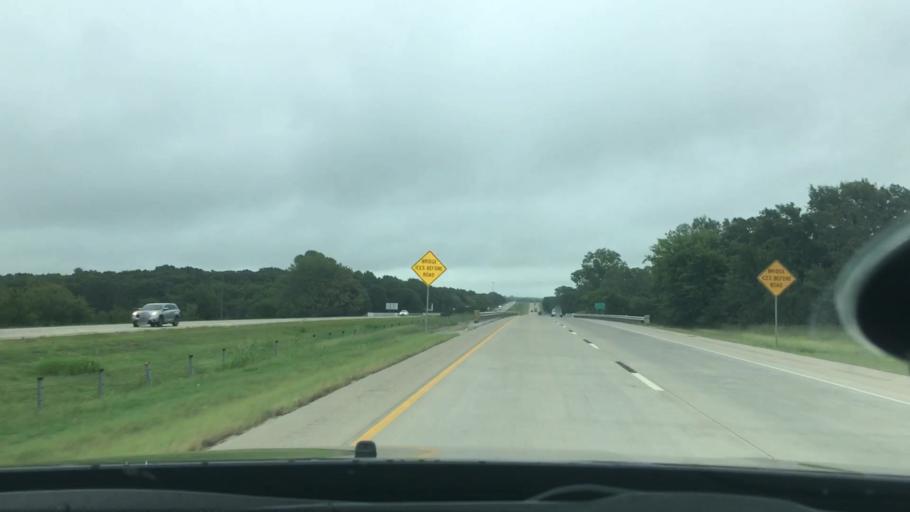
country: US
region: Oklahoma
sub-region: Okmulgee County
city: Wilson
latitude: 35.4276
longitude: -96.0901
